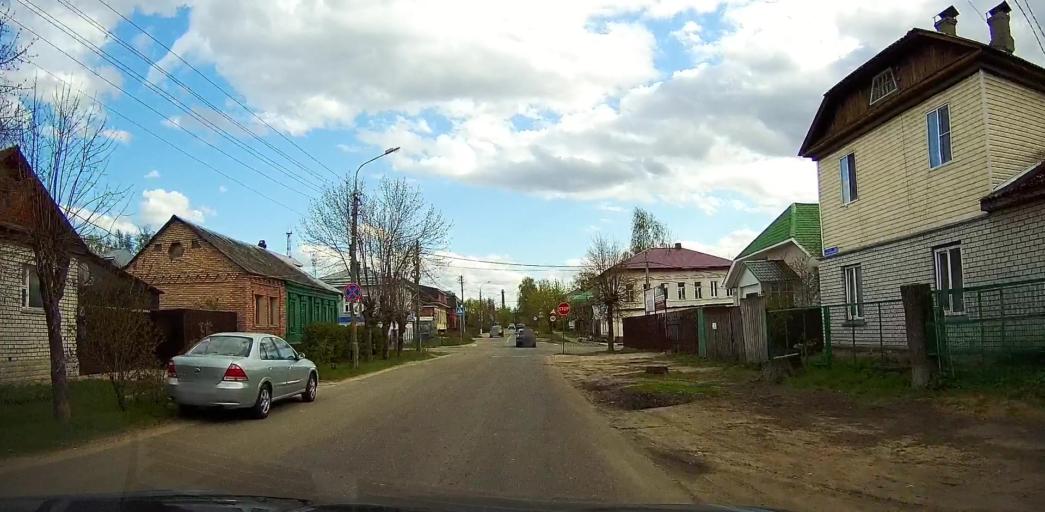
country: RU
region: Moskovskaya
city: Pavlovskiy Posad
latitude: 55.7803
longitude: 38.6472
